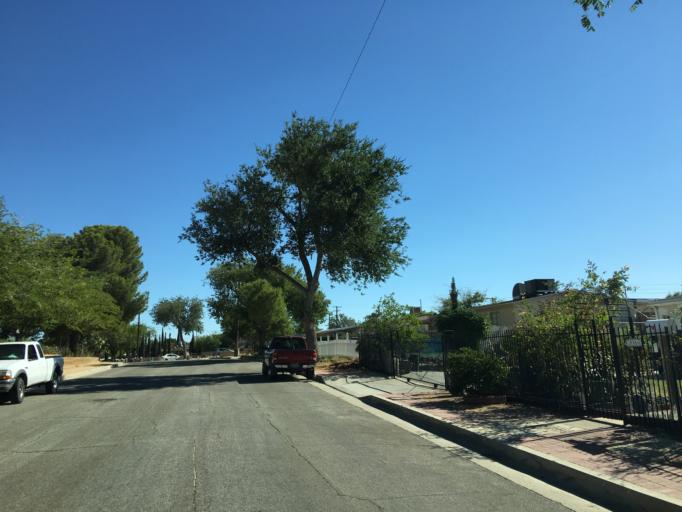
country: US
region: California
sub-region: Los Angeles County
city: Desert View Highlands
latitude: 34.5889
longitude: -118.1492
